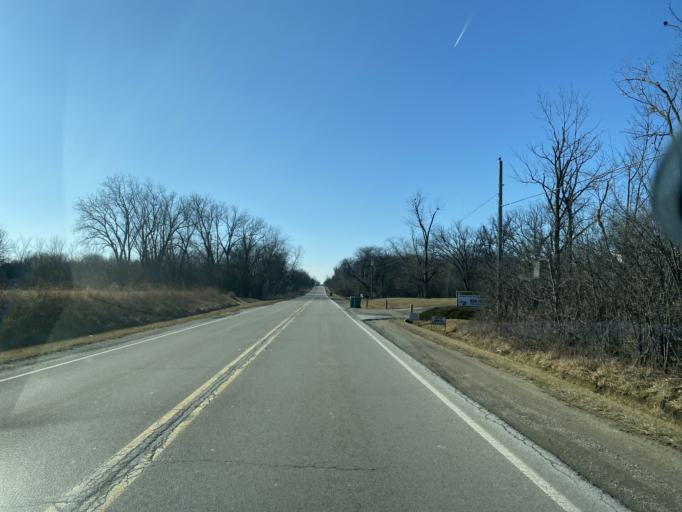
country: US
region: Illinois
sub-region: Will County
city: Goodings Grove
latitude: 41.6806
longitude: -87.9401
